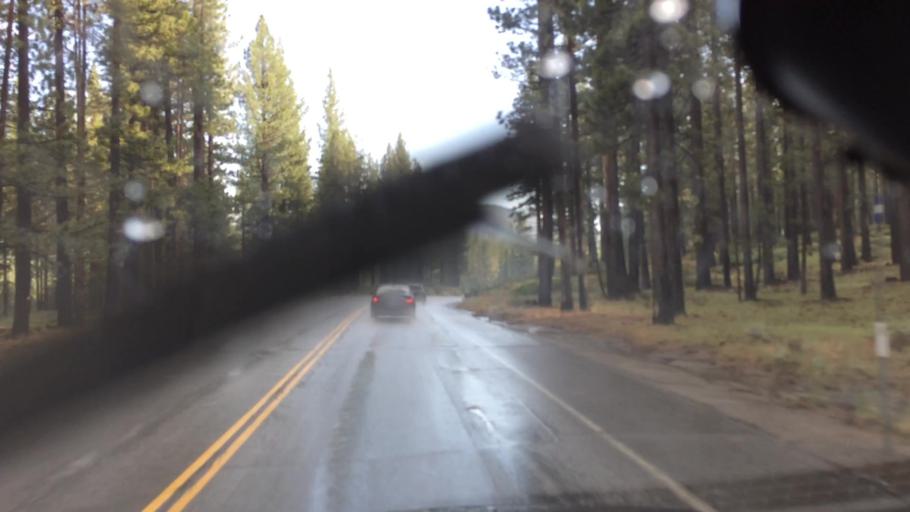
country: US
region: California
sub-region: El Dorado County
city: South Lake Tahoe
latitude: 38.9019
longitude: -119.9698
